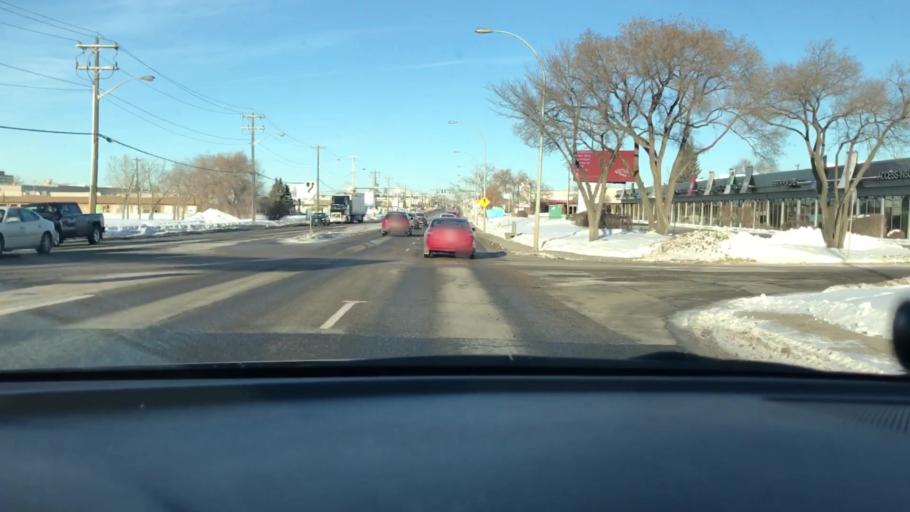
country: CA
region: Alberta
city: Edmonton
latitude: 53.4817
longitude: -113.4860
